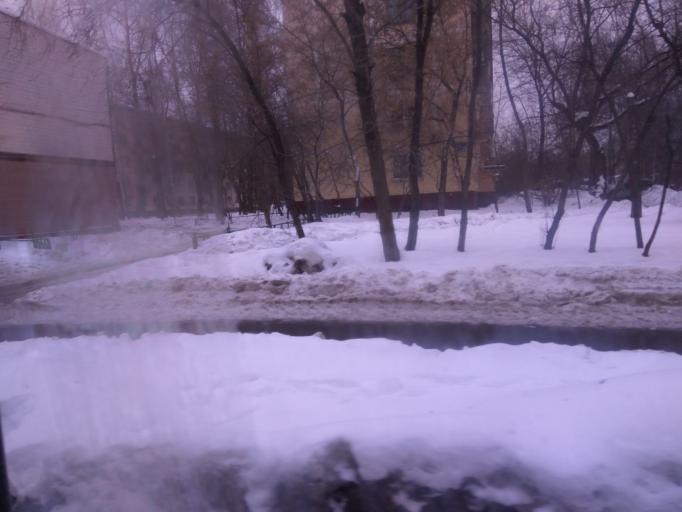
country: RU
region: Moskovskaya
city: Izmaylovo
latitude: 55.7973
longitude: 37.8180
